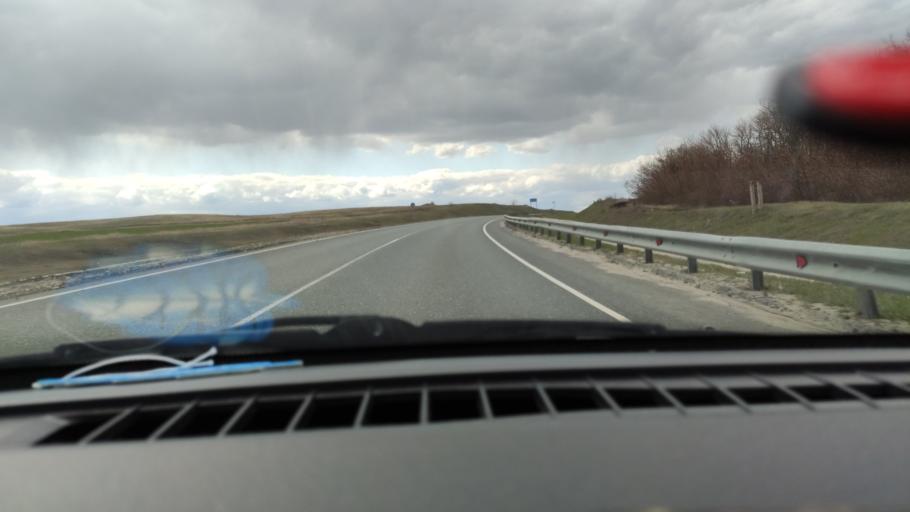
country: RU
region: Saratov
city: Alekseyevka
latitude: 52.2190
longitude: 47.8941
